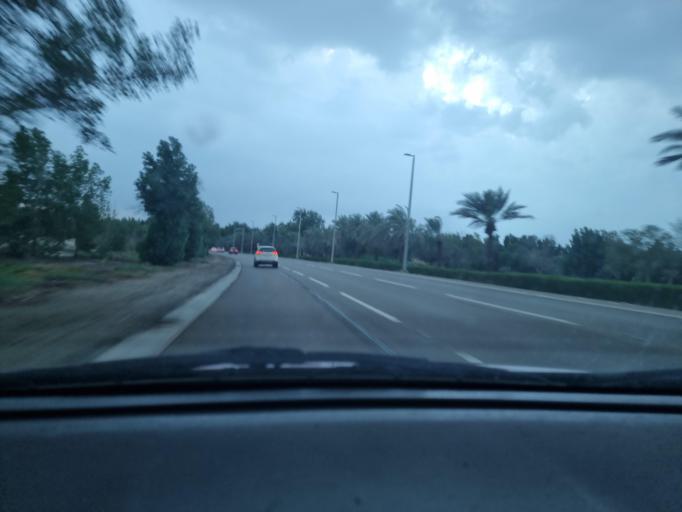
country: AE
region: Abu Dhabi
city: Abu Dhabi
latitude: 24.4136
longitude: 54.6249
